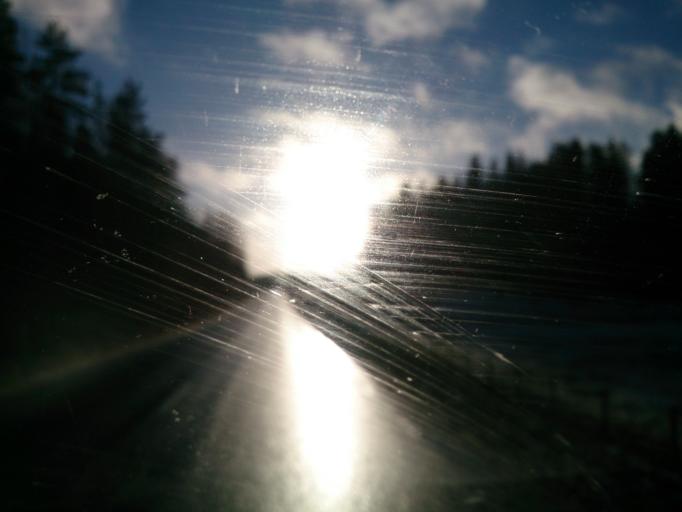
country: SE
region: OEstergoetland
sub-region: Atvidabergs Kommun
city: Atvidaberg
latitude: 58.2877
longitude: 15.8972
